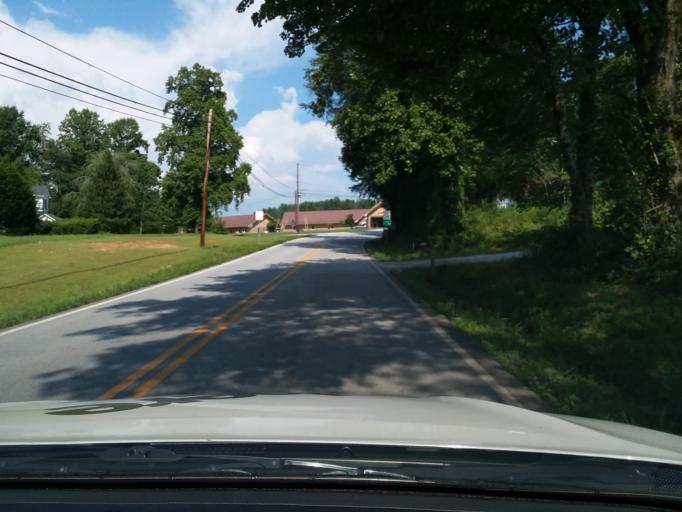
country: US
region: Georgia
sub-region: Rabun County
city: Clayton
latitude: 34.8508
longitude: -83.4399
